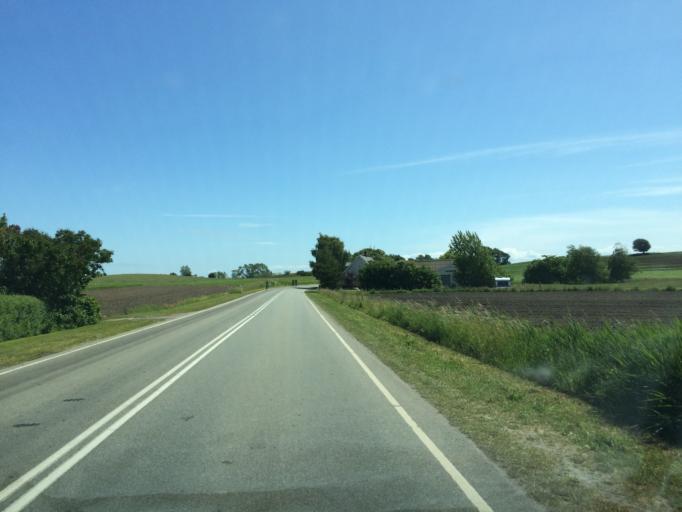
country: DK
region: Central Jutland
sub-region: Samso Kommune
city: Tranebjerg
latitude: 55.8237
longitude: 10.6025
